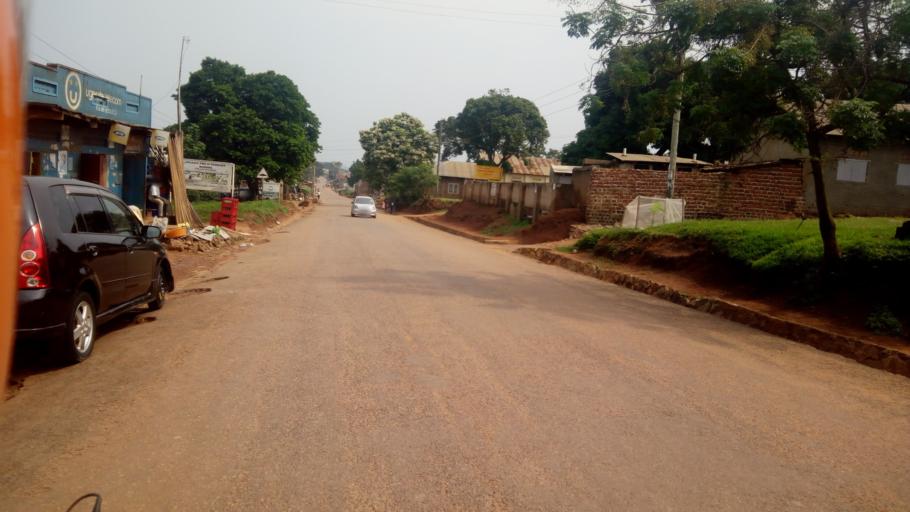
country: UG
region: Central Region
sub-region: Wakiso District
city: Kireka
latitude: 0.3077
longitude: 32.6526
